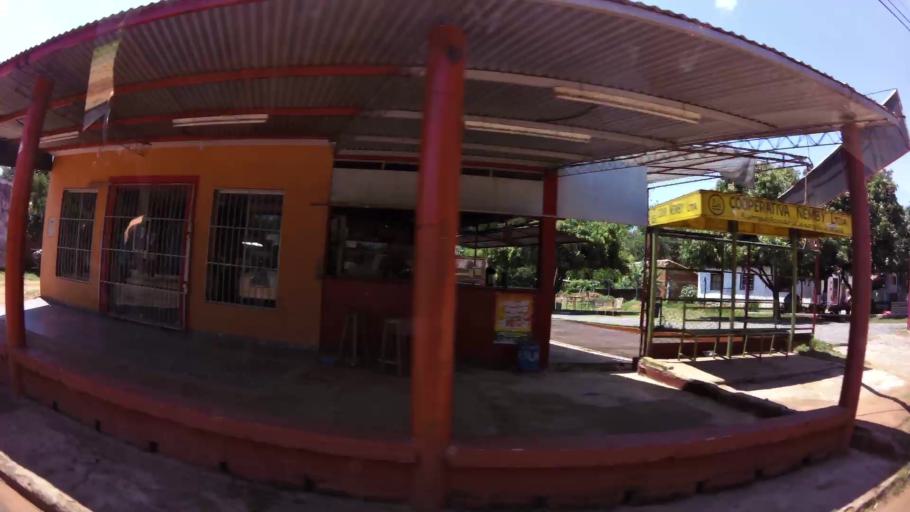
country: PY
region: Central
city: Nemby
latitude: -25.4072
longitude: -57.5261
